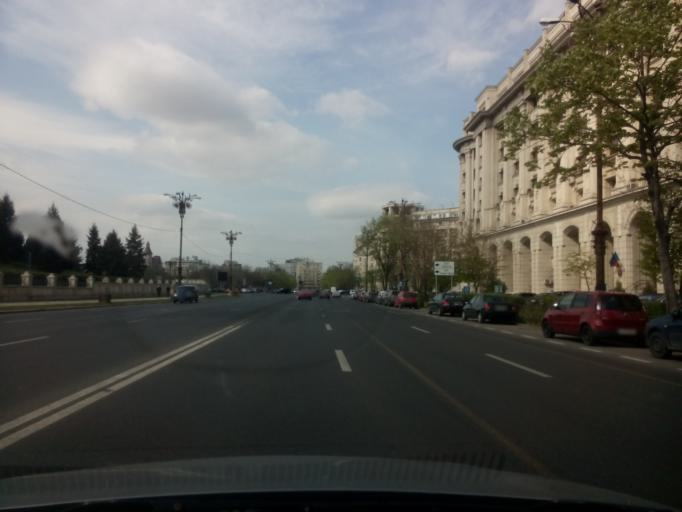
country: RO
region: Bucuresti
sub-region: Municipiul Bucuresti
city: Bucuresti
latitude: 44.4285
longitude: 26.0911
